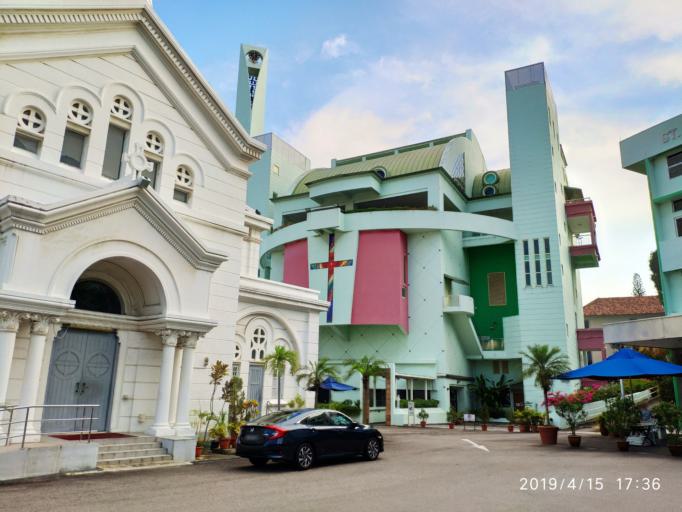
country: SG
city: Singapore
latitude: 1.2735
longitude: 103.8280
